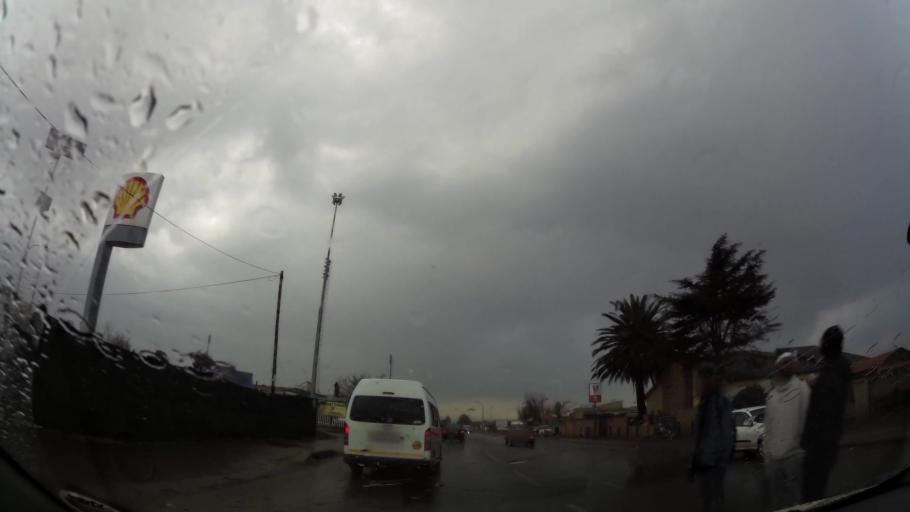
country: ZA
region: Gauteng
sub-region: Ekurhuleni Metropolitan Municipality
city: Germiston
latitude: -26.3543
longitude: 28.1316
